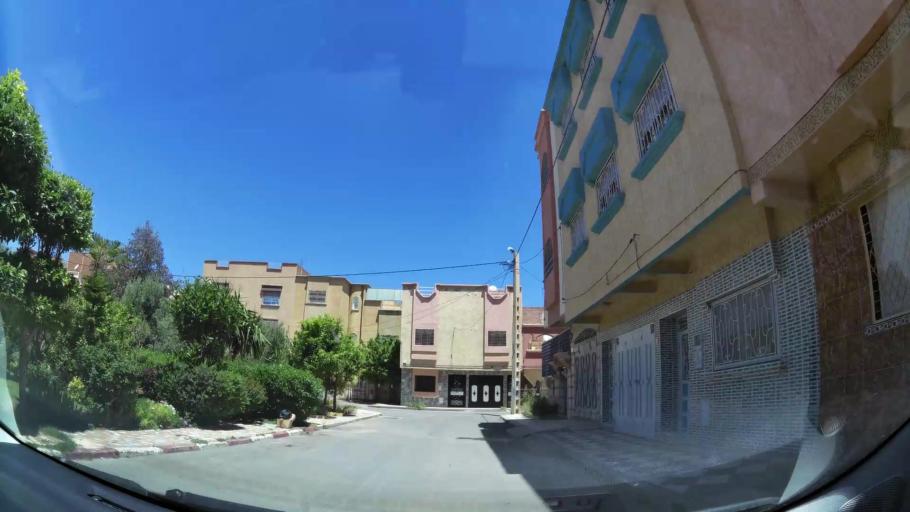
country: MA
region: Oriental
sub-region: Oujda-Angad
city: Oujda
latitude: 34.6732
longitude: -1.8848
